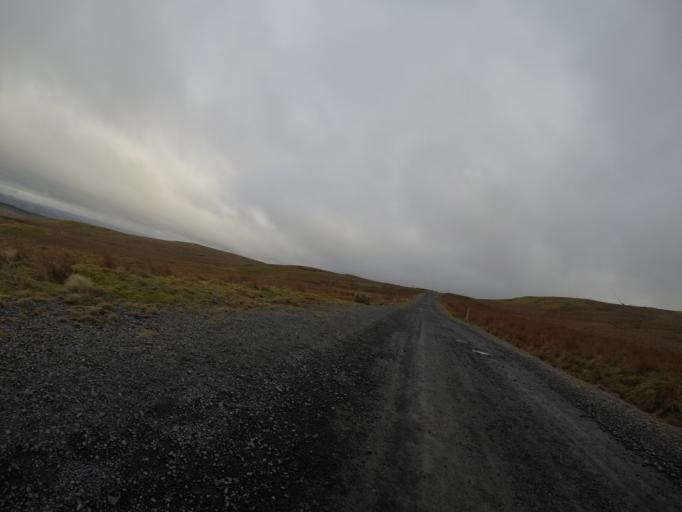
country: GB
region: Scotland
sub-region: North Ayrshire
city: Fairlie
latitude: 55.7628
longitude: -4.7923
